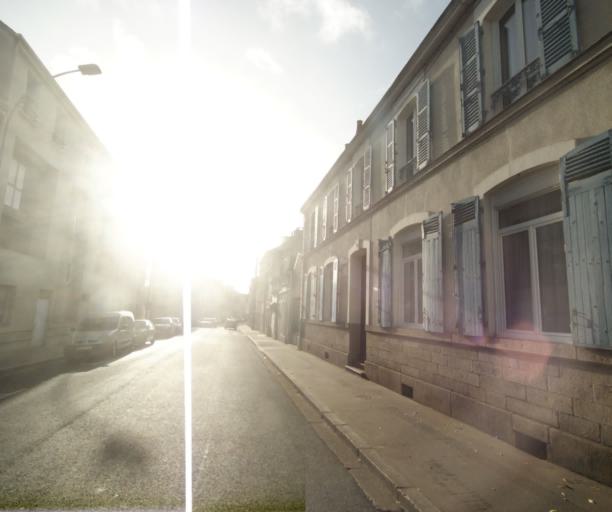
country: FR
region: Pays de la Loire
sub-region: Departement de la Sarthe
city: Le Mans
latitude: 47.9979
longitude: 0.1983
